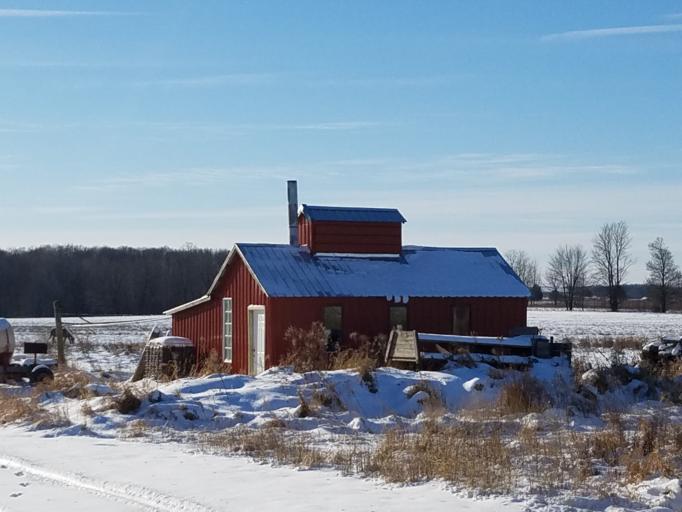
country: US
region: Wisconsin
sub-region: Clark County
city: Loyal
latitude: 44.6262
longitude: -90.4224
